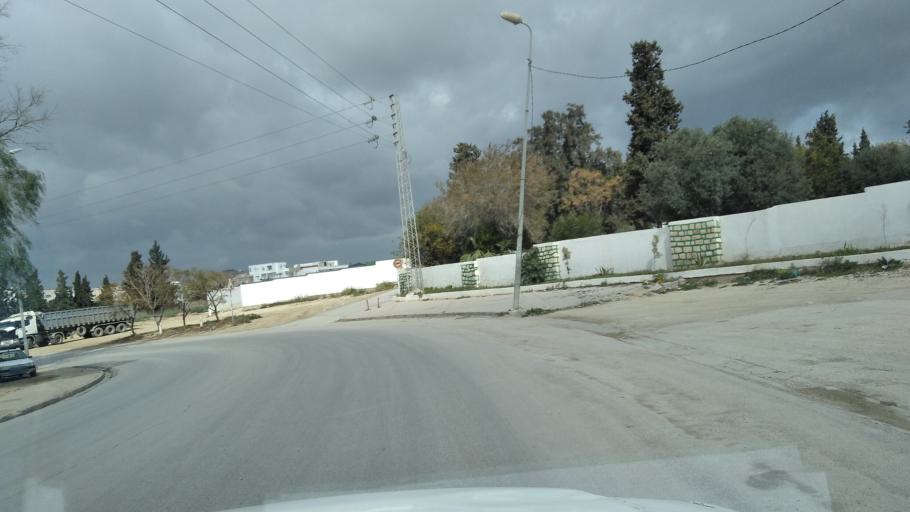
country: TN
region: Bin 'Arus
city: Ben Arous
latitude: 36.7441
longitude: 10.2284
